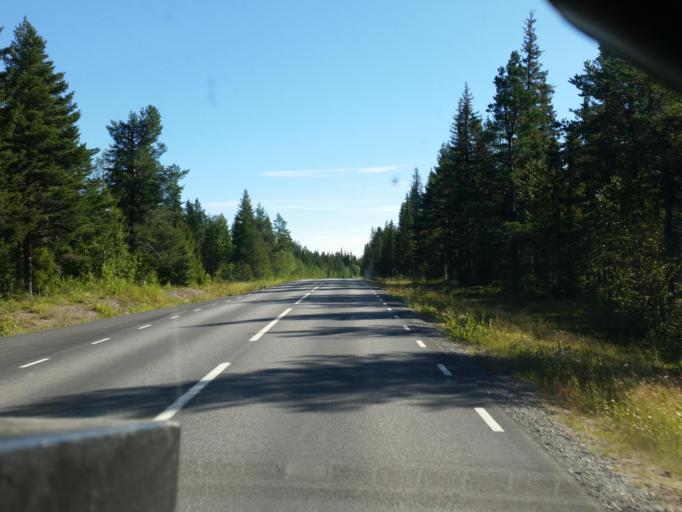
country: SE
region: Vaesterbotten
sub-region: Skelleftea Kommun
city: Storvik
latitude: 65.3264
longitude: 20.7377
